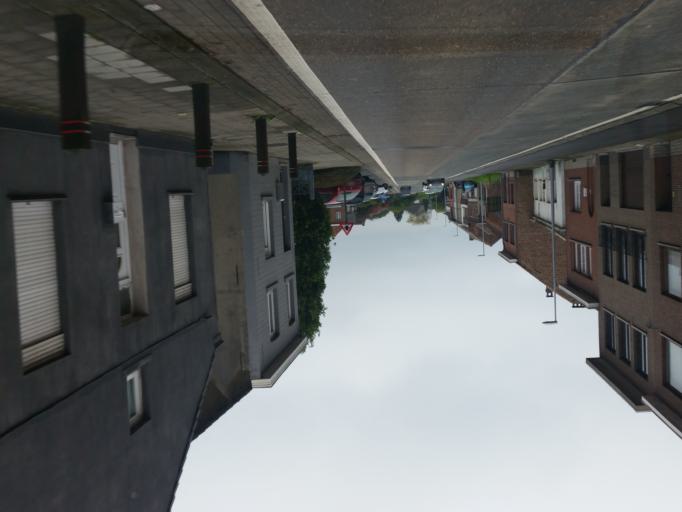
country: BE
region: Flanders
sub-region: Provincie Vlaams-Brabant
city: Sint-Pieters-Leeuw
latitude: 50.7868
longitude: 4.2689
